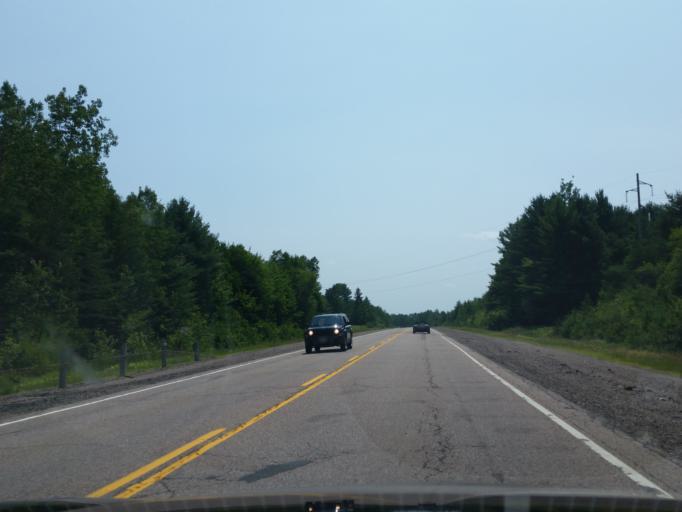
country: CA
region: Ontario
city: Petawawa
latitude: 45.8549
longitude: -77.2833
